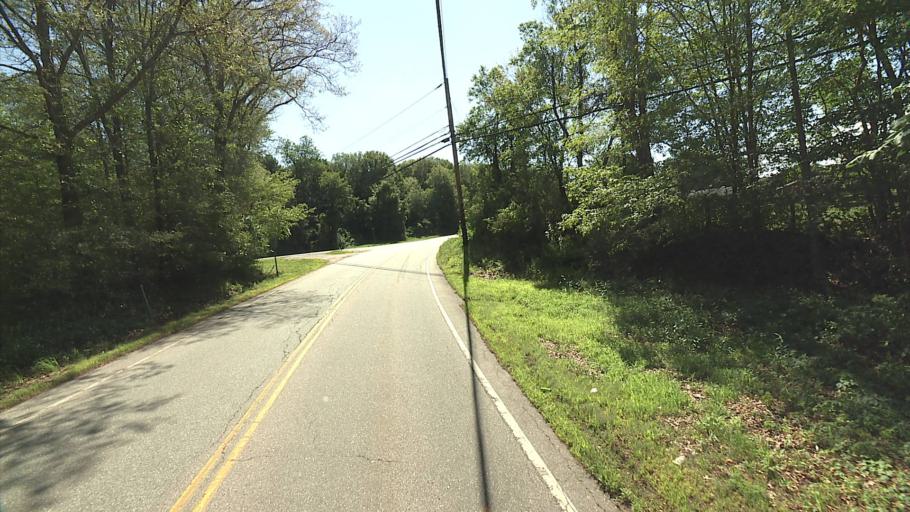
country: US
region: Connecticut
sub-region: New London County
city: Colchester
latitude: 41.5982
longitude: -72.2937
